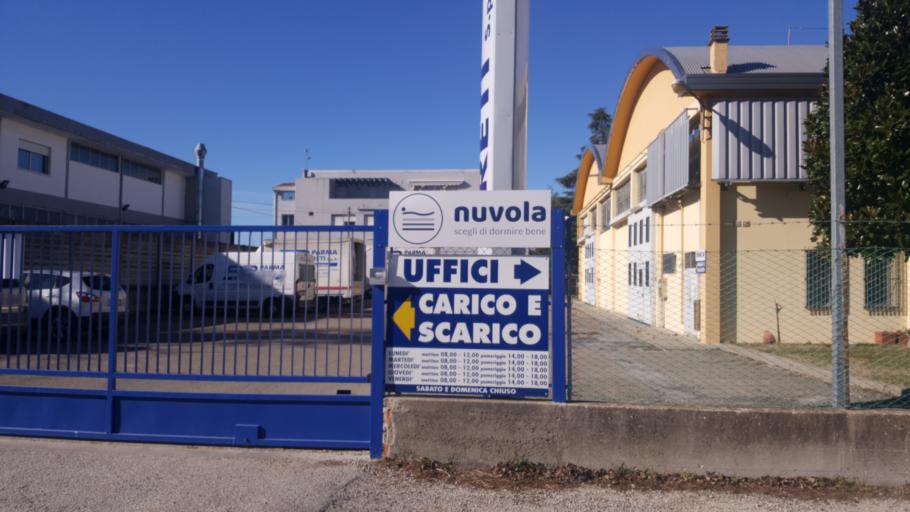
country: IT
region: Emilia-Romagna
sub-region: Provincia di Rimini
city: Cerasolo
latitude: 43.9930
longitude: 12.5386
